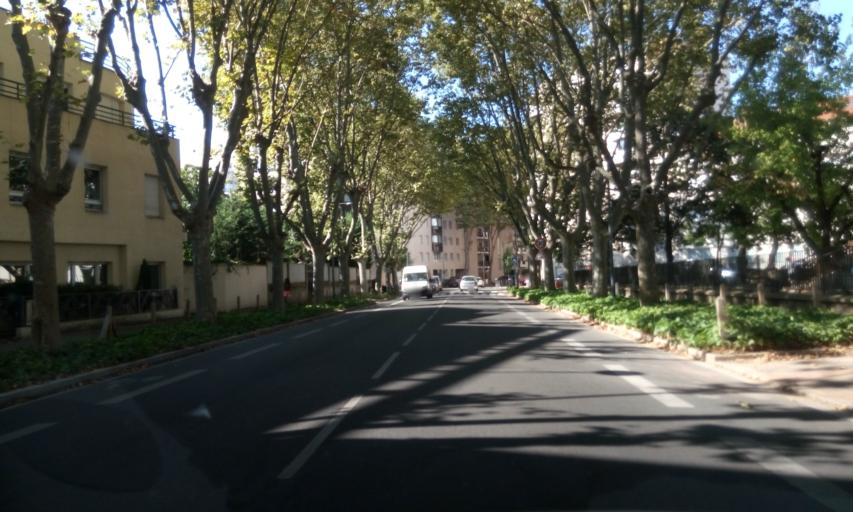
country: FR
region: Rhone-Alpes
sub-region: Departement du Rhone
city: Villeurbanne
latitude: 45.7611
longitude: 4.8746
